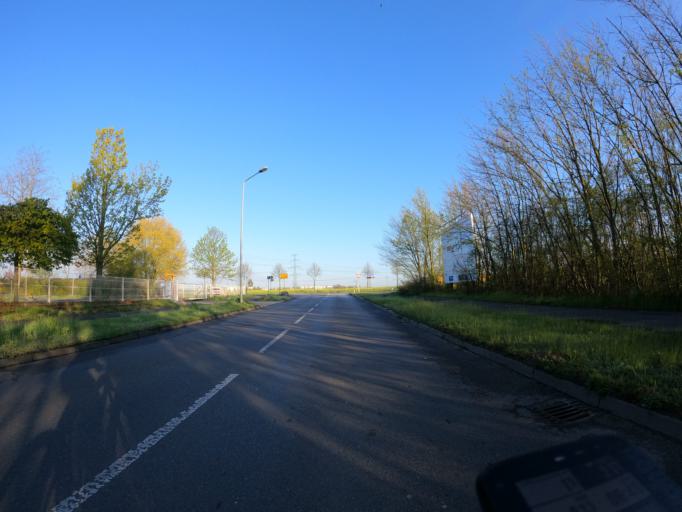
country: DE
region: Brandenburg
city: Neuenhagen
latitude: 52.5443
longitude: 13.7082
